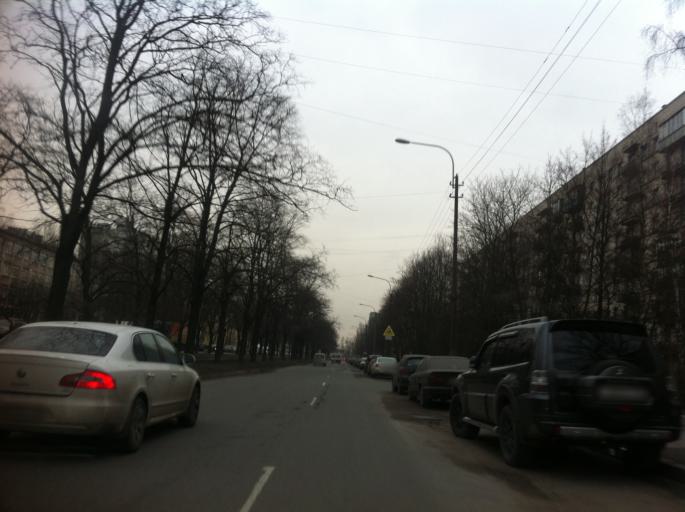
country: RU
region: St.-Petersburg
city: Dachnoye
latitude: 59.8425
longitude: 30.2674
